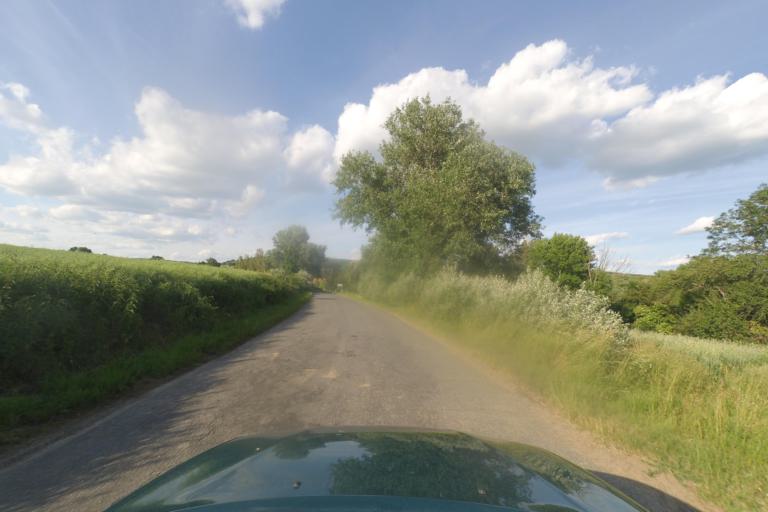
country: PL
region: Lower Silesian Voivodeship
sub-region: Powiat dzierzoniowski
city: Niemcza
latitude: 50.6912
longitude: 16.8477
